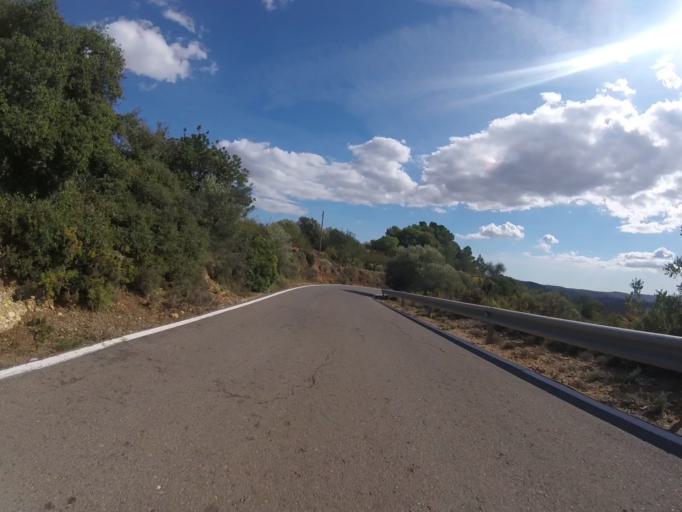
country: ES
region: Valencia
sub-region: Provincia de Castello
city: Cuevas de Vinroma
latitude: 40.3782
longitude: 0.1120
